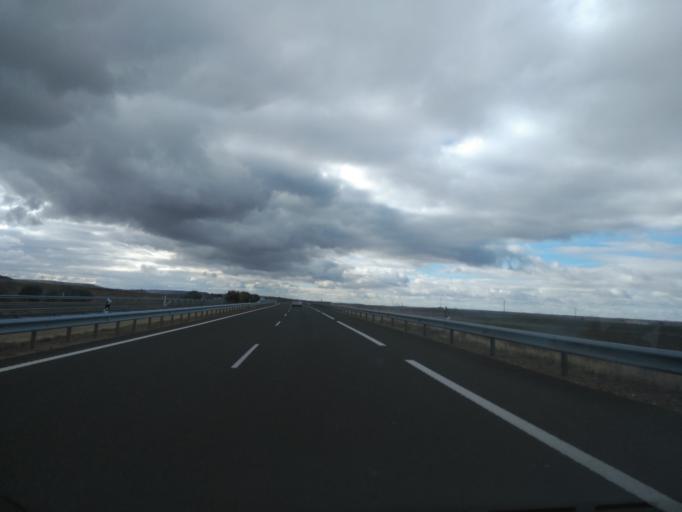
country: ES
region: Castille and Leon
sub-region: Provincia de Palencia
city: Amusco
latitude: 42.1686
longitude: -4.4594
